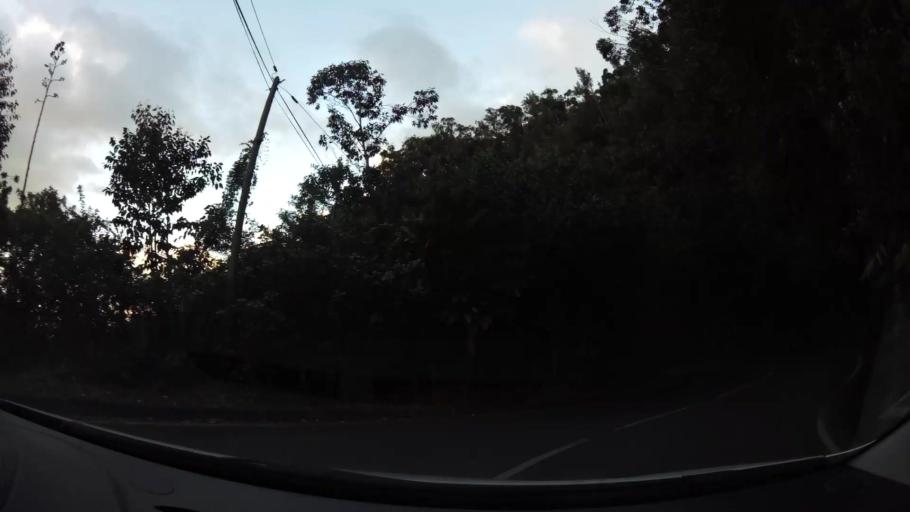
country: RE
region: Reunion
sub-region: Reunion
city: Saint-Denis
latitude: -20.9214
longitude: 55.4527
